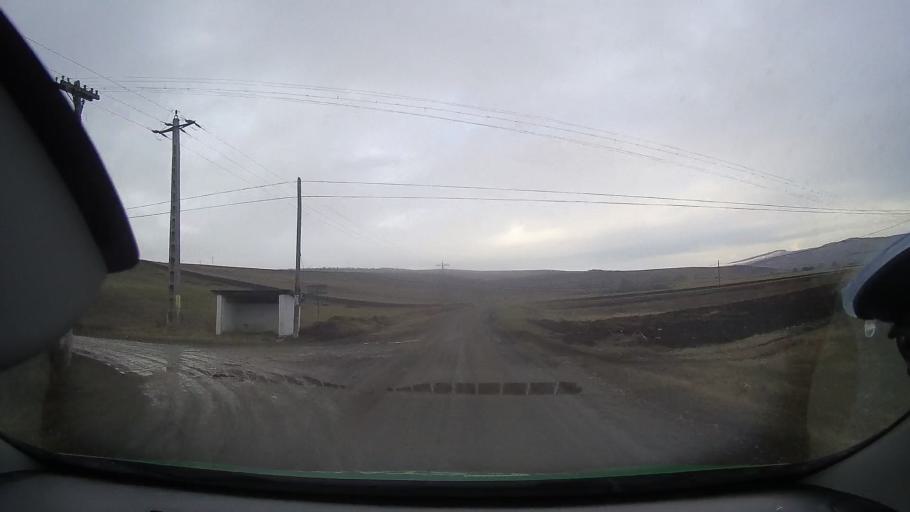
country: RO
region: Mures
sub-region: Comuna Bichis
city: Bichis
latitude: 46.3840
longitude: 24.0801
